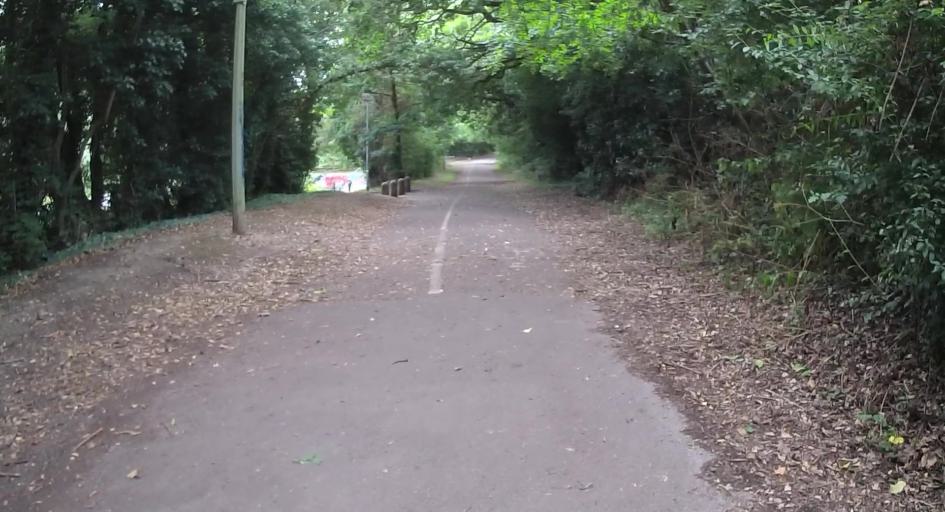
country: GB
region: England
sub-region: Wokingham
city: Lower Earley
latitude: 51.4270
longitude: -0.9277
